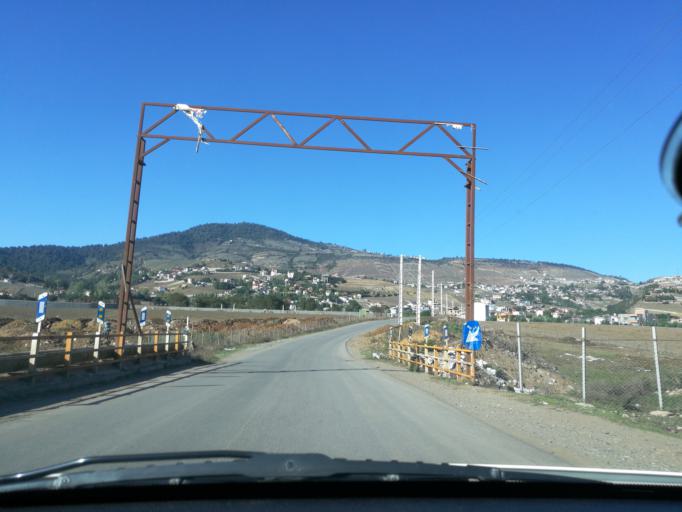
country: IR
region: Mazandaran
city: `Abbasabad
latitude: 36.5418
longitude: 51.1822
